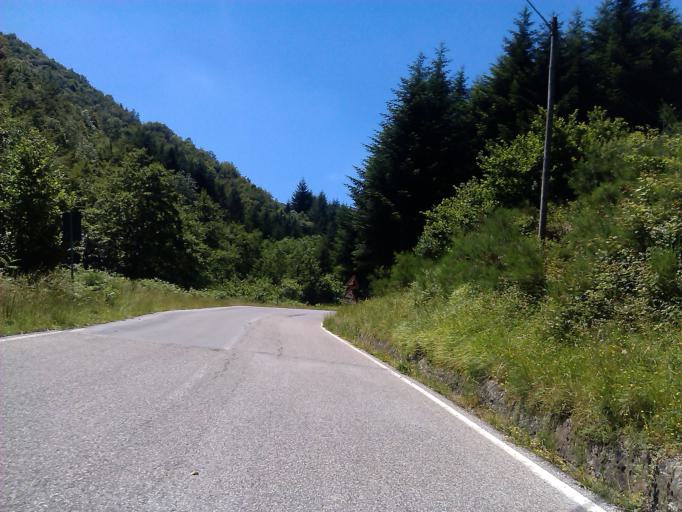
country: IT
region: Tuscany
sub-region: Provincia di Prato
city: Cantagallo
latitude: 44.0288
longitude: 11.0380
